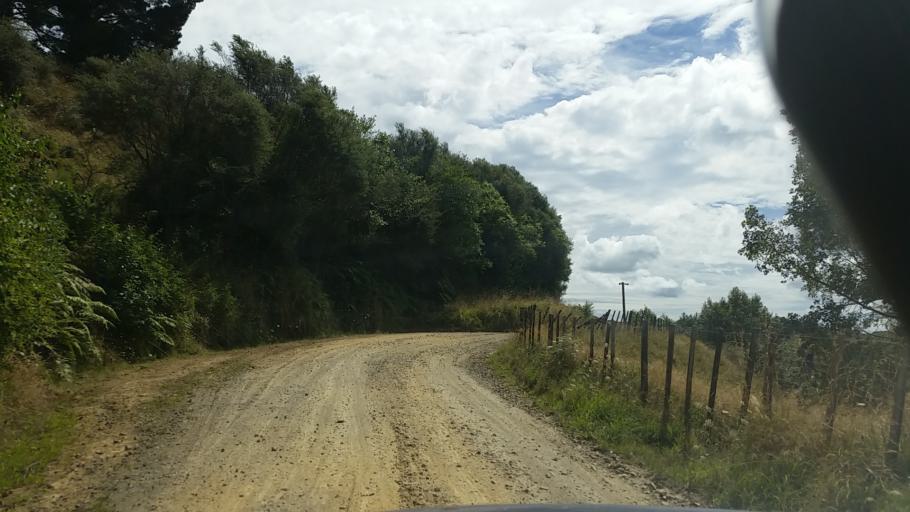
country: NZ
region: Taranaki
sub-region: South Taranaki District
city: Eltham
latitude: -39.2507
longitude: 174.5654
